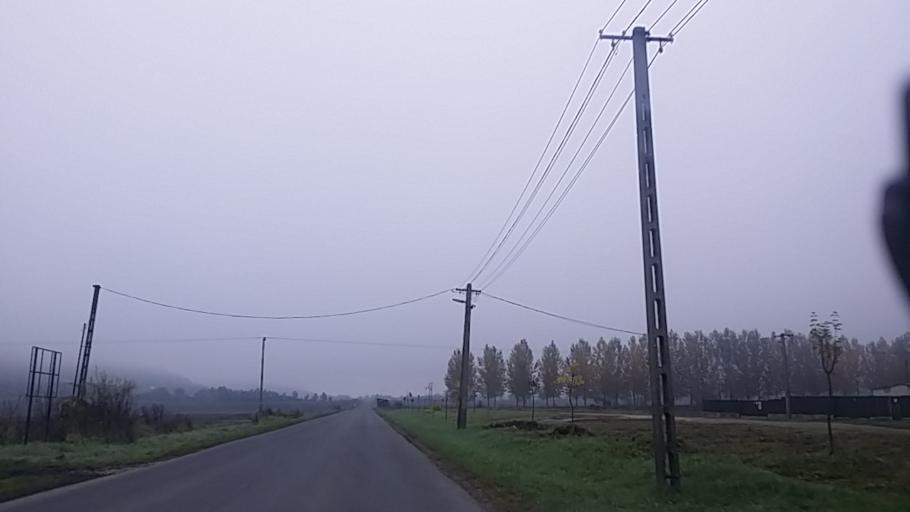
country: HU
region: Borsod-Abauj-Zemplen
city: Sajokaza
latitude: 48.2349
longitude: 20.5123
